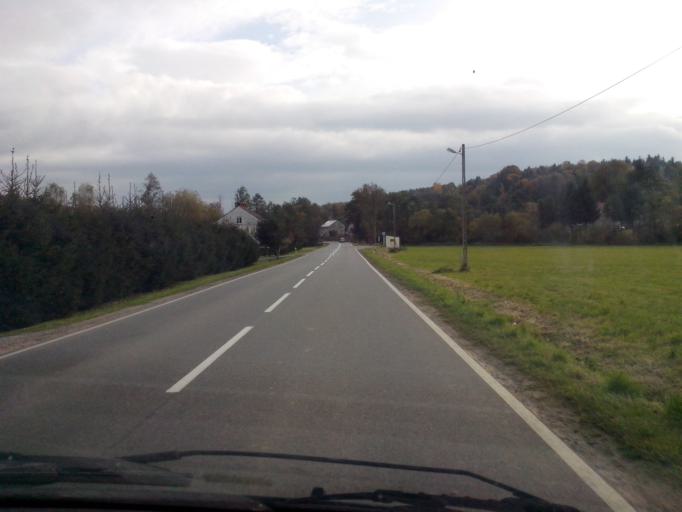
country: PL
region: Subcarpathian Voivodeship
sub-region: Powiat strzyzowski
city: Wisniowa
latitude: 49.8914
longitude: 21.6436
